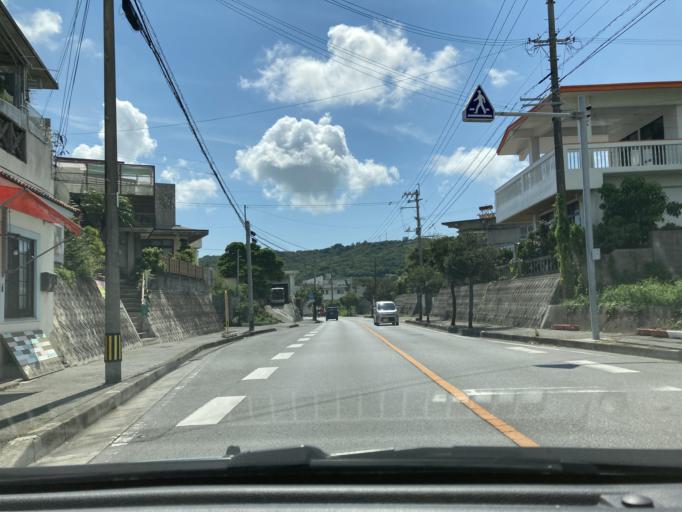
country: JP
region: Okinawa
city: Tomigusuku
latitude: 26.1647
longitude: 127.7555
